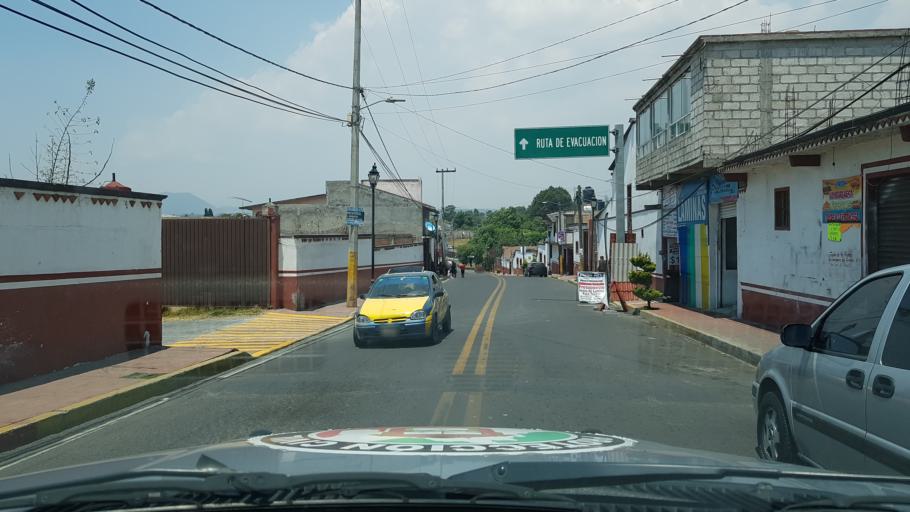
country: MX
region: Mexico
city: Ozumba de Alzate
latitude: 19.0339
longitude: -98.7988
